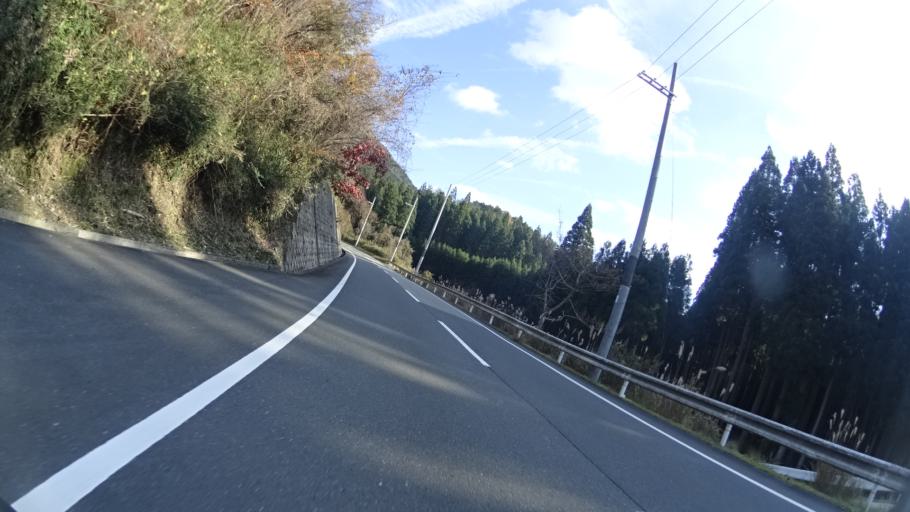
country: JP
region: Kyoto
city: Kameoka
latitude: 35.1219
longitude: 135.5603
